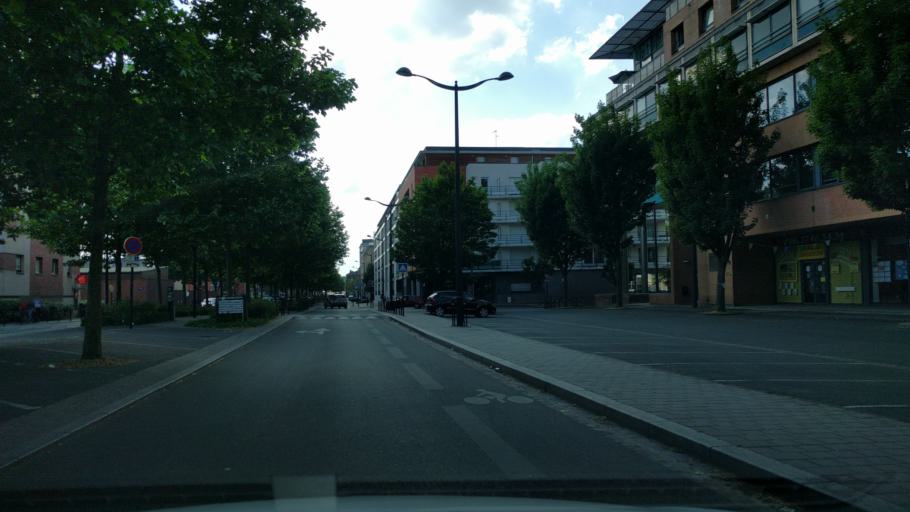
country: FR
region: Nord-Pas-de-Calais
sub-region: Departement du Nord
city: Valenciennes
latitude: 50.3641
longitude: 3.5278
